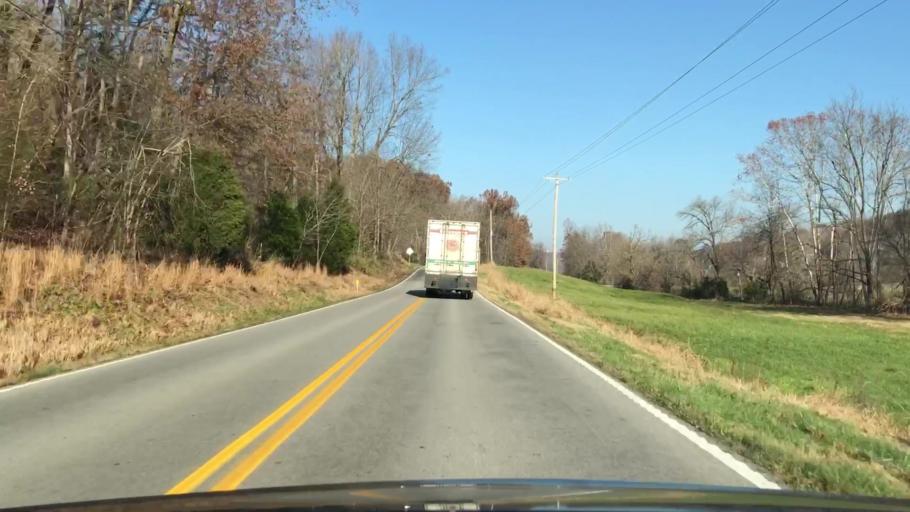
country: US
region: Kentucky
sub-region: Grayson County
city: Leitchfield
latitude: 37.4385
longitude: -86.2838
